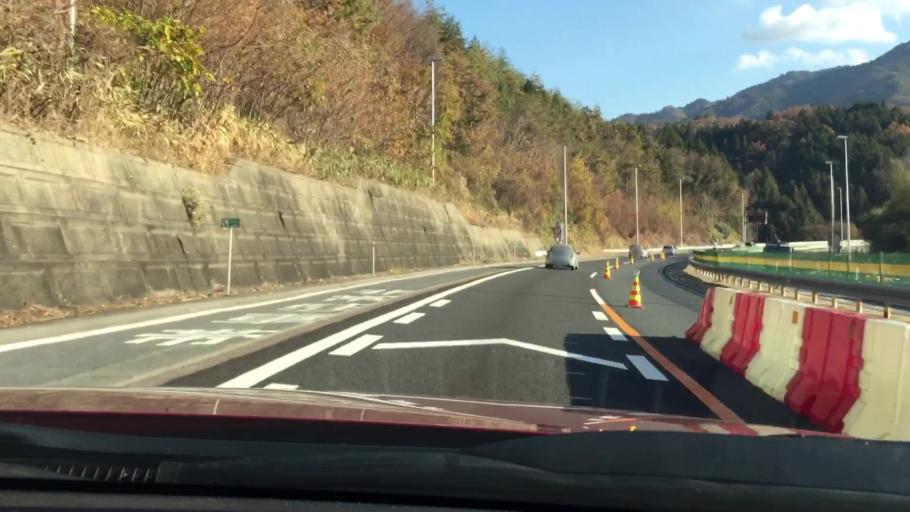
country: JP
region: Gifu
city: Nakatsugawa
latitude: 35.5176
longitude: 137.5640
